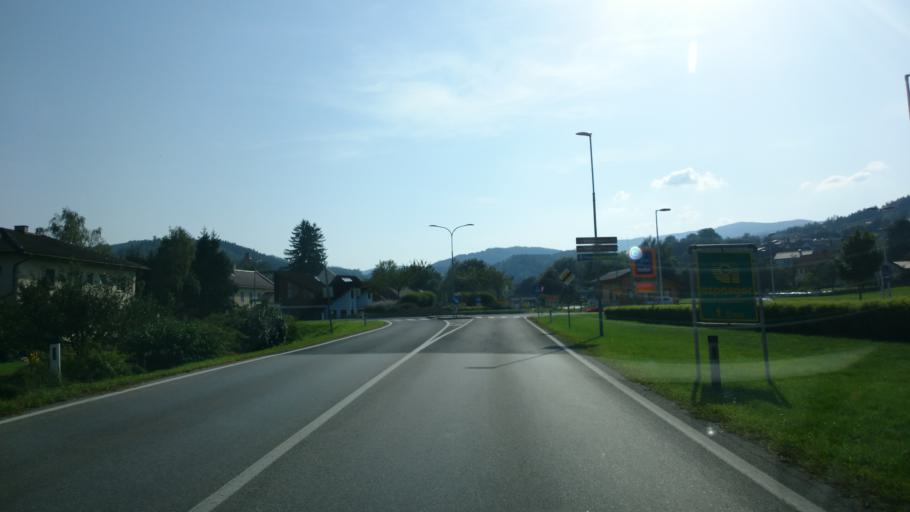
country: AT
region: Lower Austria
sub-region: Politischer Bezirk Neunkirchen
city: Thomasberg
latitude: 47.5601
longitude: 16.0941
